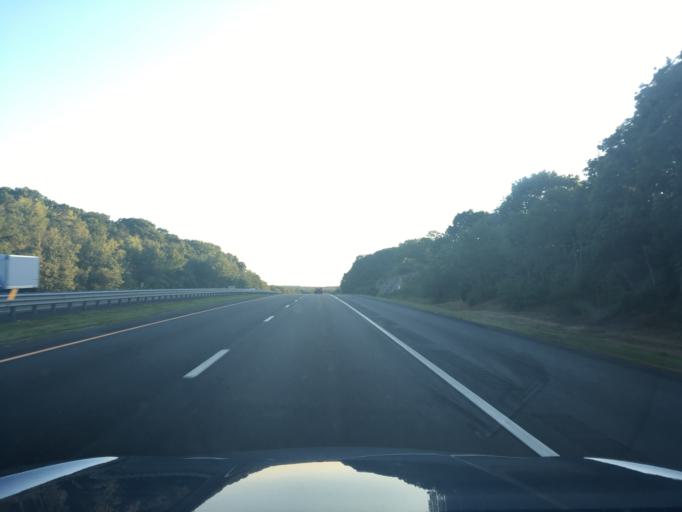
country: US
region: Rhode Island
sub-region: Kent County
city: West Warwick
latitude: 41.6638
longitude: -71.5205
